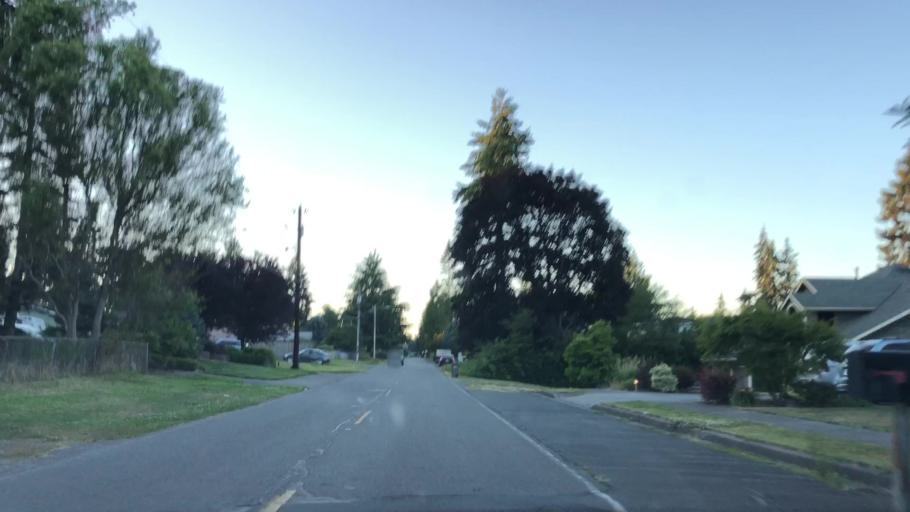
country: US
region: Washington
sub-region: Snohomish County
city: Brier
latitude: 47.7854
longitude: -122.2720
